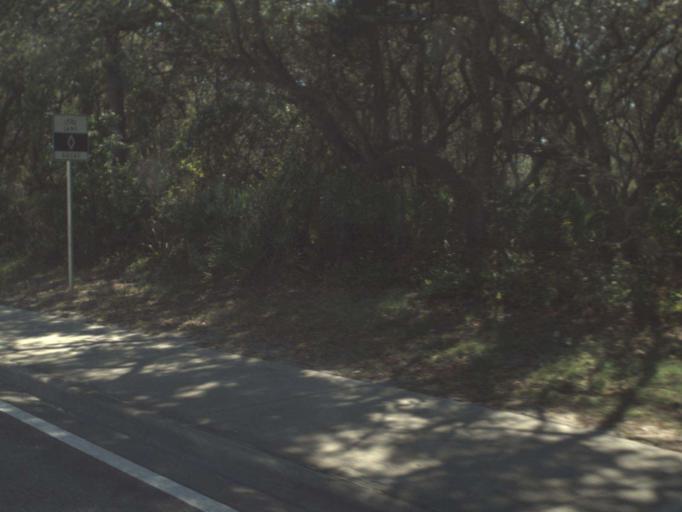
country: US
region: Florida
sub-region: Walton County
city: Miramar Beach
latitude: 30.3783
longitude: -86.3153
